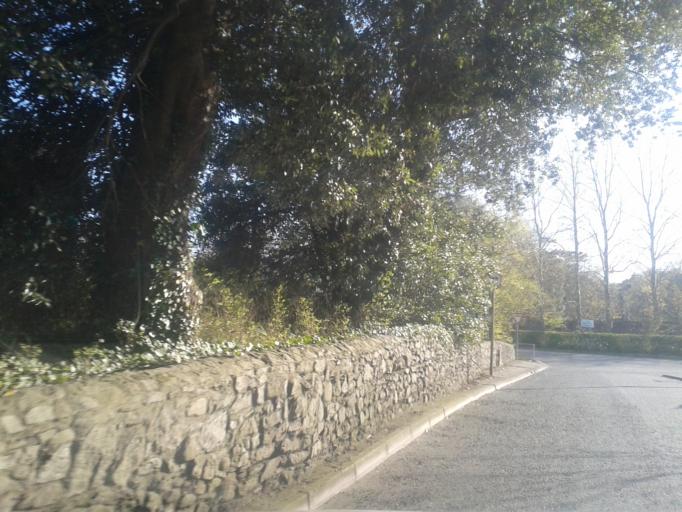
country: IE
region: Leinster
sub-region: Fingal County
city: Swords
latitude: 53.4619
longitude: -6.2124
